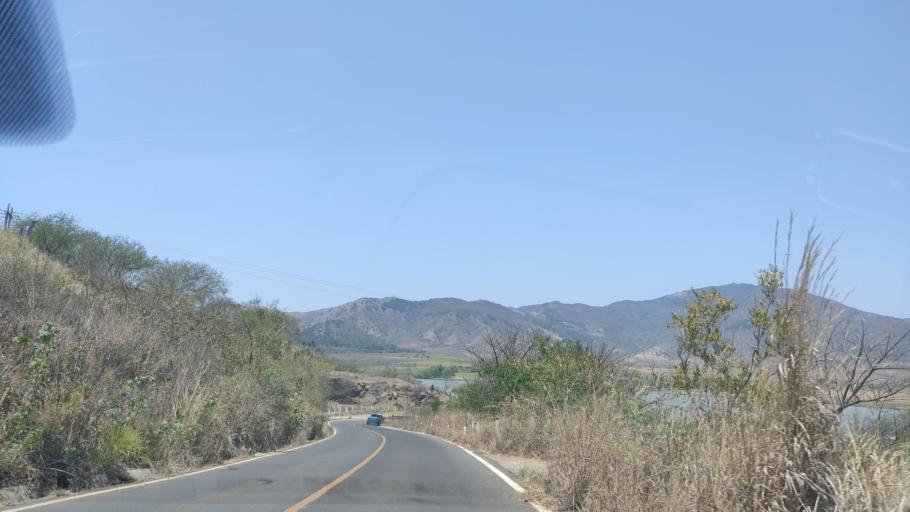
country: MX
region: Nayarit
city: Puga
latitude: 21.6055
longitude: -104.7389
